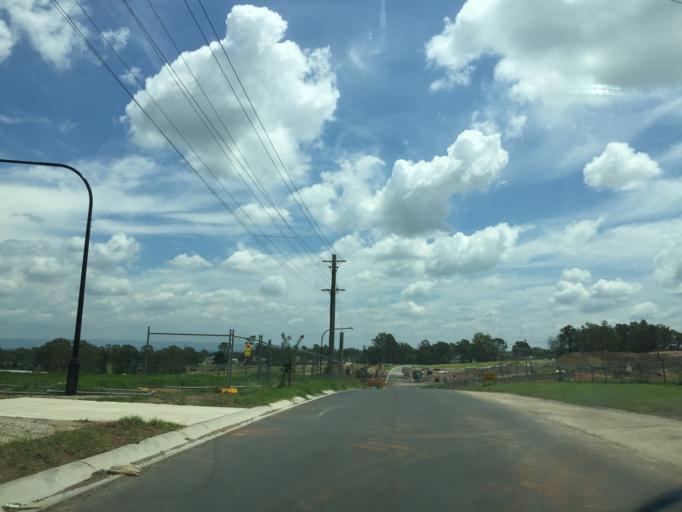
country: AU
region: New South Wales
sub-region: Blacktown
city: Riverstone
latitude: -33.6915
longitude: 150.8801
